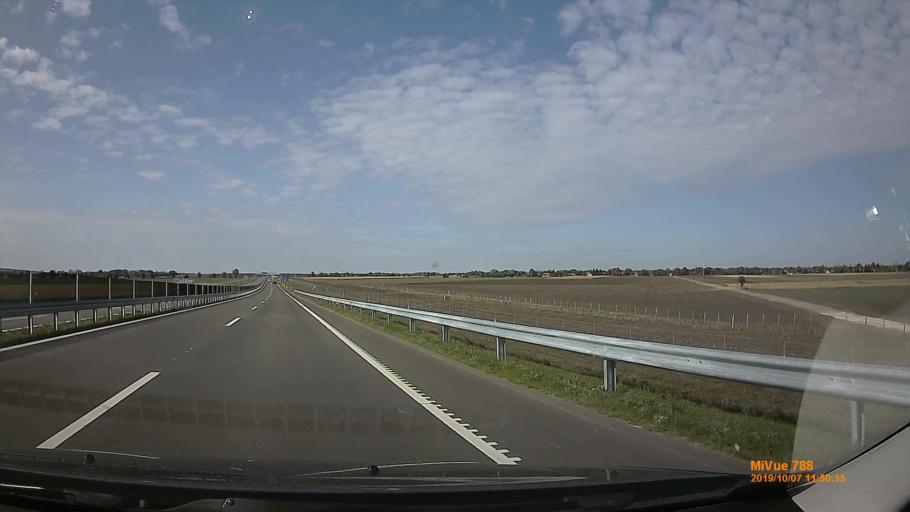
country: HU
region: Bekes
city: Szarvas
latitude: 46.8129
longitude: 20.6659
